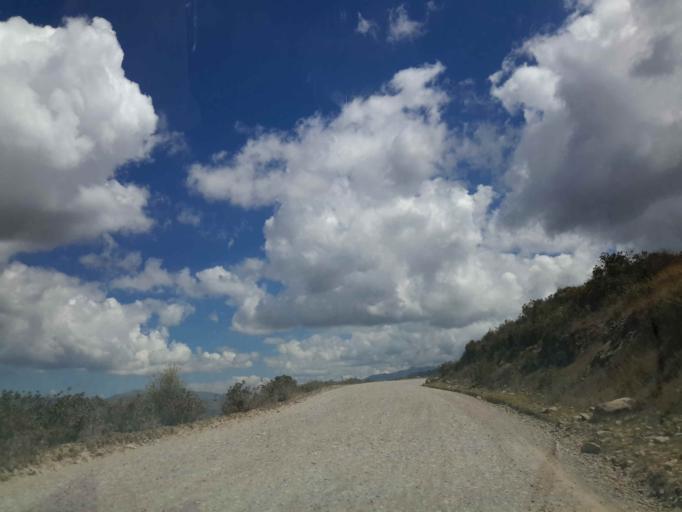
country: PE
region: Apurimac
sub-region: Provincia de Andahuaylas
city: San Jeronimo
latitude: -13.6389
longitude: -73.3364
